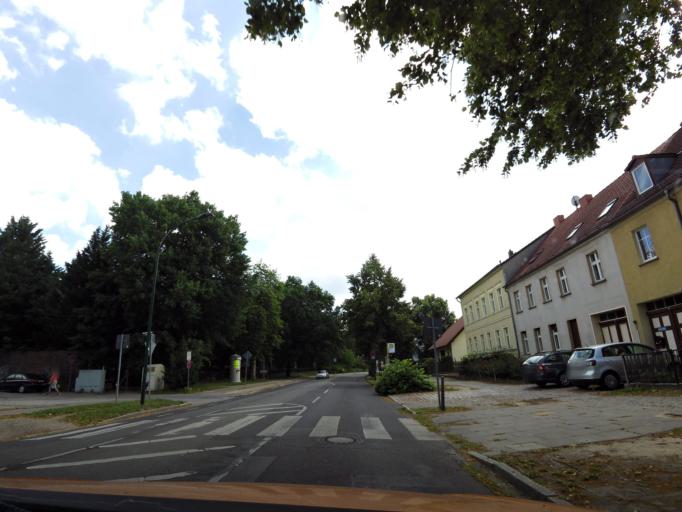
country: DE
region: Brandenburg
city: Nauen
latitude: 52.6077
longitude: 12.8684
